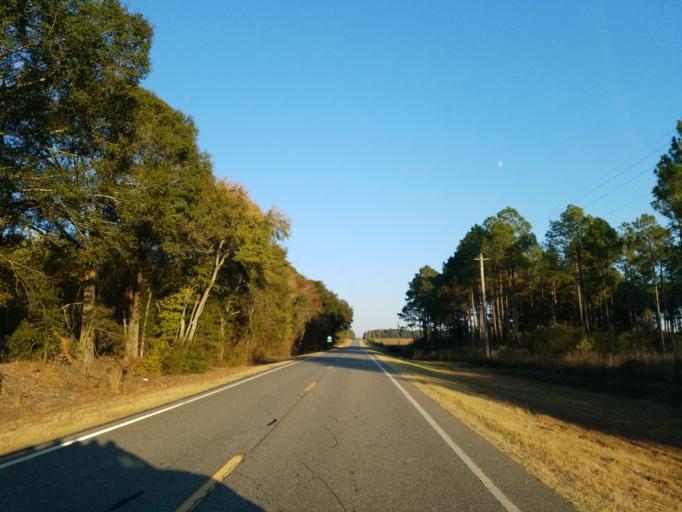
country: US
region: Georgia
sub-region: Turner County
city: Ashburn
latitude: 31.8596
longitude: -83.6316
